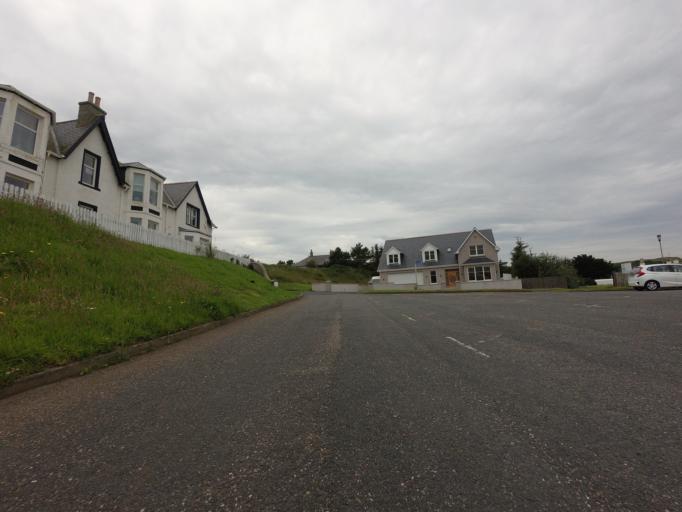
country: GB
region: Scotland
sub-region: Aberdeenshire
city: Banff
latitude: 57.6692
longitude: -2.5531
